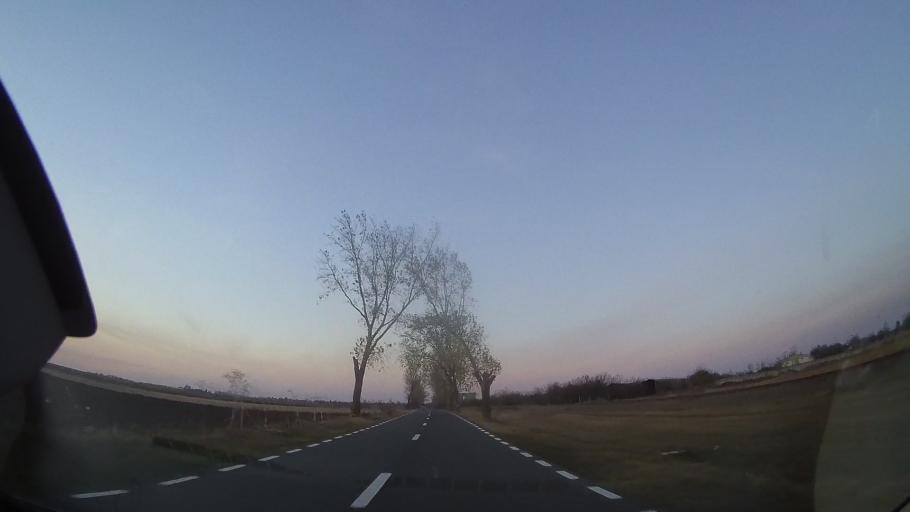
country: RO
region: Constanta
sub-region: Comuna Cobadin
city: Cobadin
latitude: 44.0435
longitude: 28.2545
